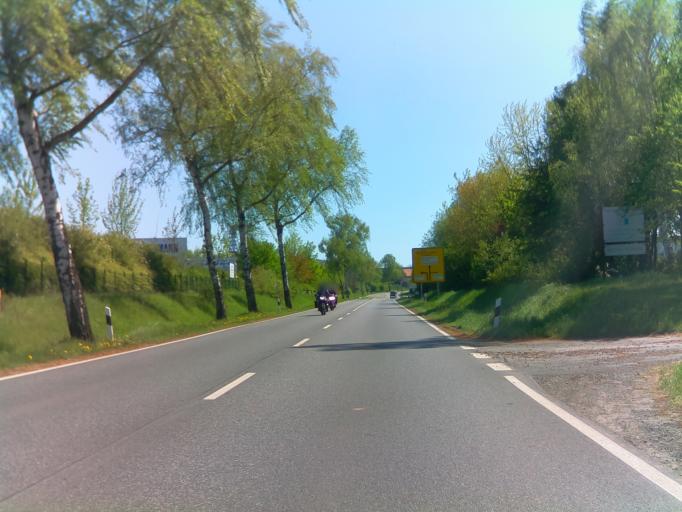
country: DE
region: Hesse
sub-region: Regierungsbezirk Giessen
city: Alsfeld
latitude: 50.7503
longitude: 9.2866
